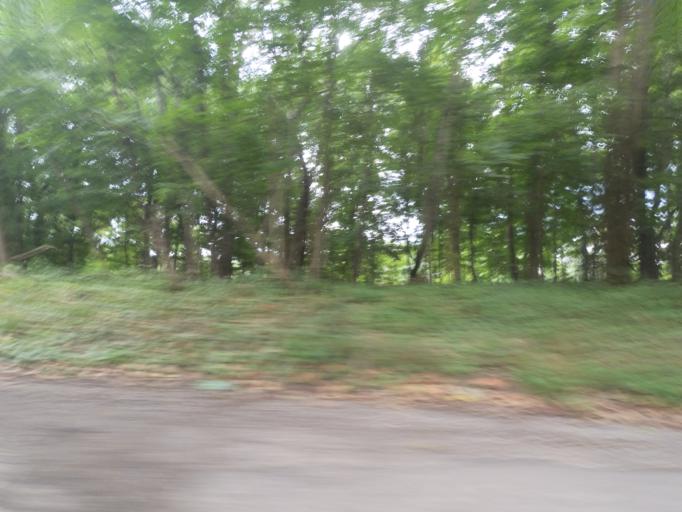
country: US
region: West Virginia
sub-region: Cabell County
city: Huntington
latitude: 38.3857
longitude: -82.4213
